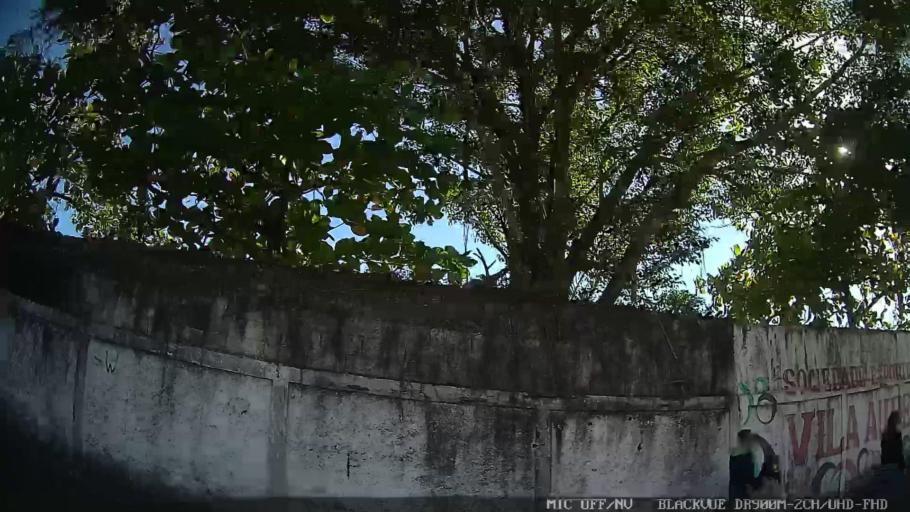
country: BR
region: Sao Paulo
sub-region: Guaruja
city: Guaruja
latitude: -23.9459
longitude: -46.2809
